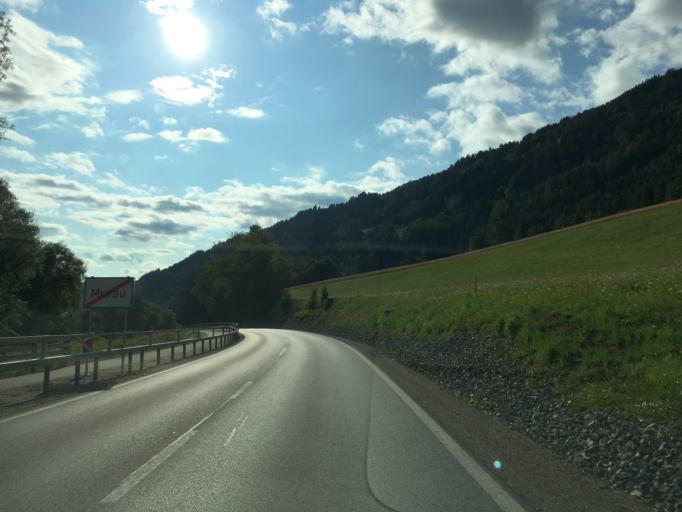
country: AT
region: Styria
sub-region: Politischer Bezirk Murau
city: Murau
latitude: 47.1135
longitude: 14.1600
